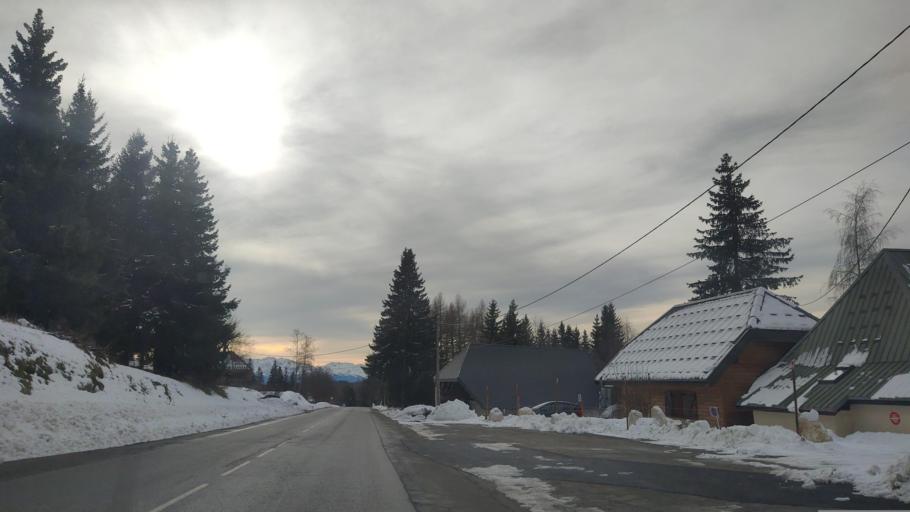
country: FR
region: Rhone-Alpes
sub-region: Departement de la Savoie
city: Mery
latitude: 45.6460
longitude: 5.9865
